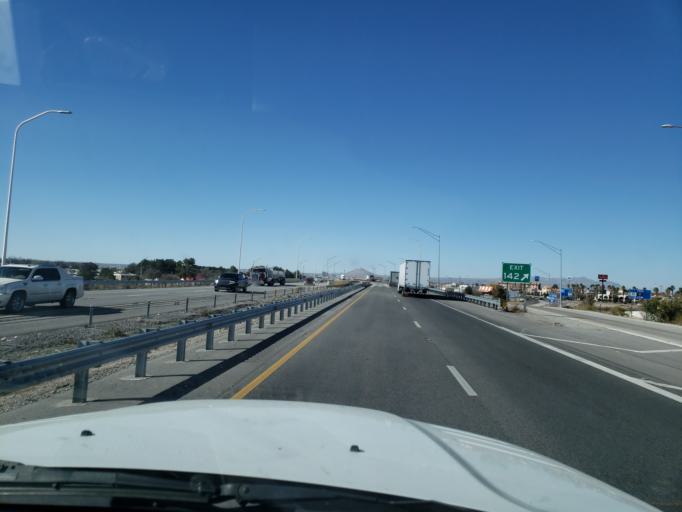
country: US
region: New Mexico
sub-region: Dona Ana County
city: University Park
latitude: 32.2787
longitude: -106.7645
